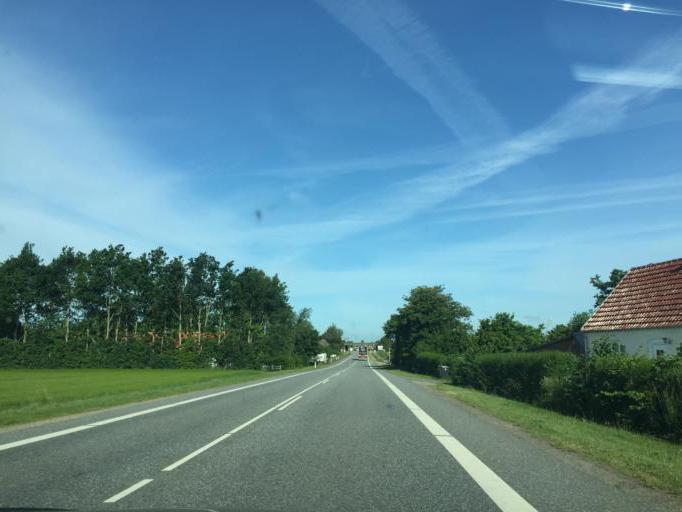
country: DK
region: South Denmark
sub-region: Middelfart Kommune
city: Norre Aby
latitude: 55.4670
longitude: 9.9060
